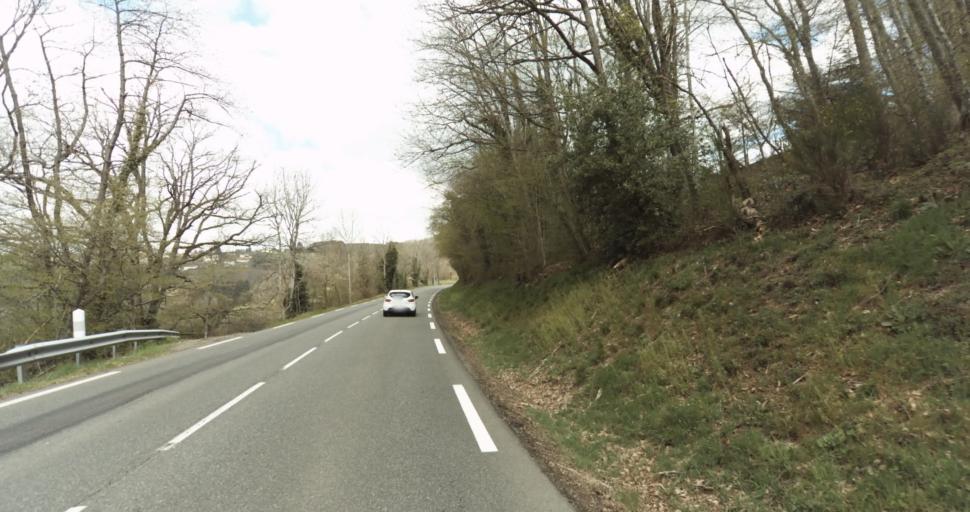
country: FR
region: Rhone-Alpes
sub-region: Departement du Rhone
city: Tarare
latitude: 45.9265
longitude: 4.4004
